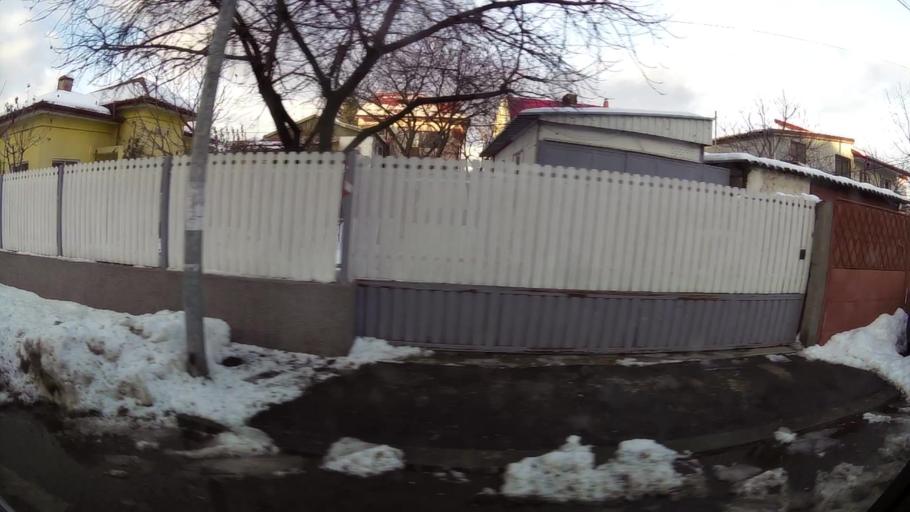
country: RO
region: Ilfov
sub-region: Comuna Popesti-Leordeni
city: Popesti-Leordeni
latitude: 44.3725
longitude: 26.1383
